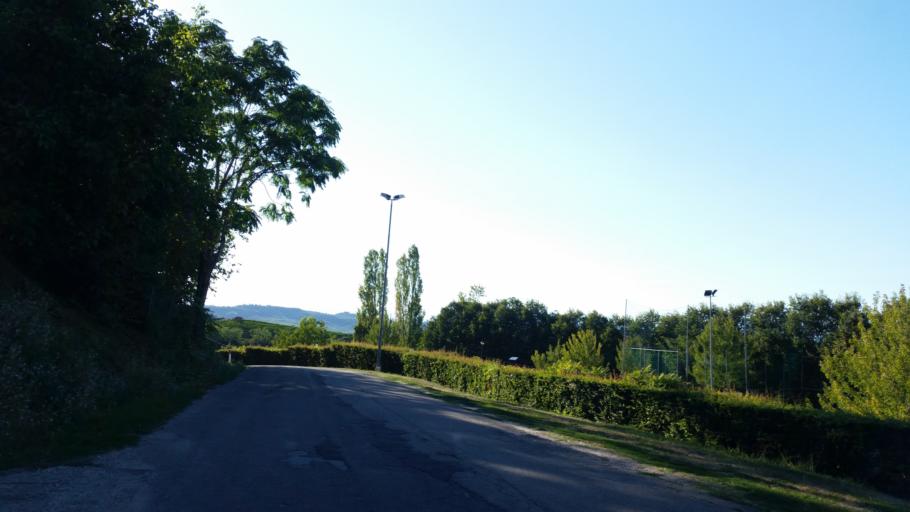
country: IT
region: Piedmont
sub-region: Provincia di Cuneo
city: Neive-Borgonovo
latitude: 44.7273
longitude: 8.1142
